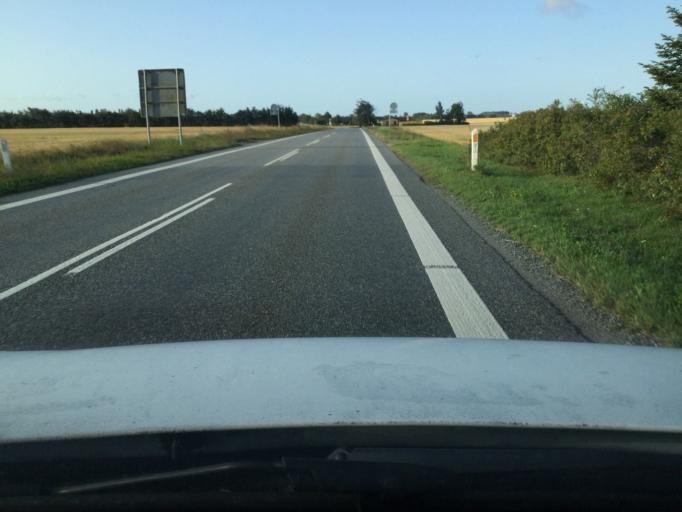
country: DK
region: Zealand
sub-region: Lolland Kommune
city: Rodby
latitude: 54.7203
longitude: 11.3845
